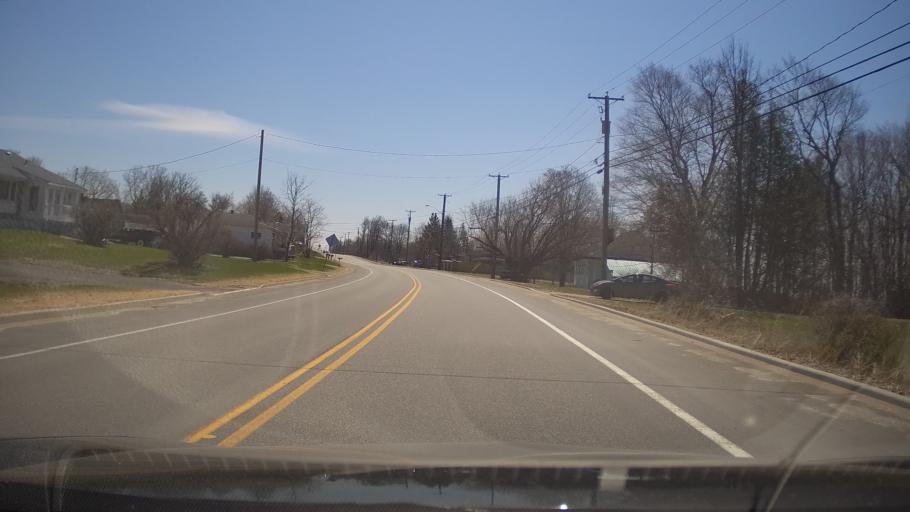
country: CA
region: Ontario
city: Bells Corners
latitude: 45.4433
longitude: -75.9190
